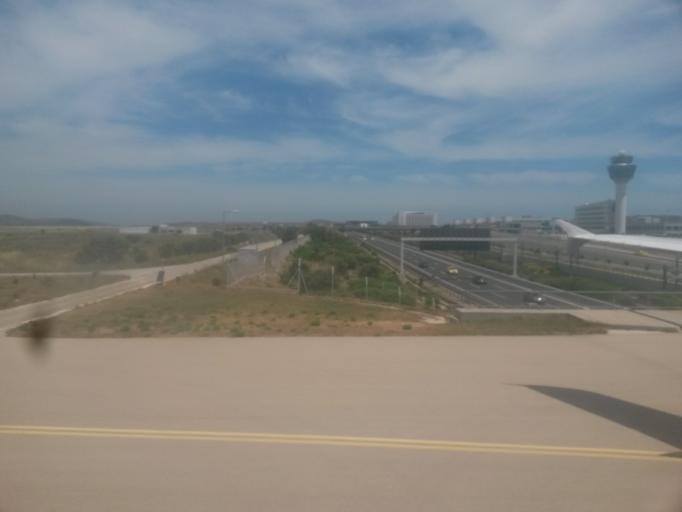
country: GR
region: Attica
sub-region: Nomarchia Anatolikis Attikis
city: Spata
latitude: 37.9316
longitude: 23.9388
